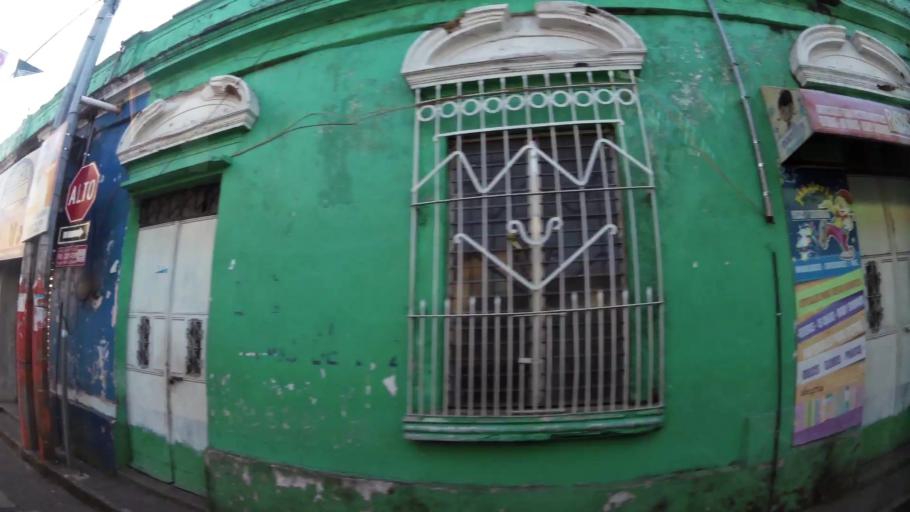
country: GT
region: Suchitepeque
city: Mazatenango
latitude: 14.5324
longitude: -91.5042
